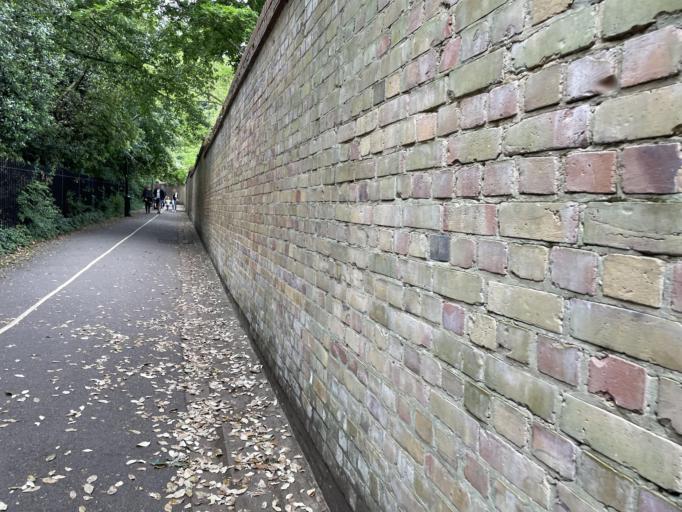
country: GB
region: England
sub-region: Greater London
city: Kensington
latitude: 51.5044
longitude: -0.2019
